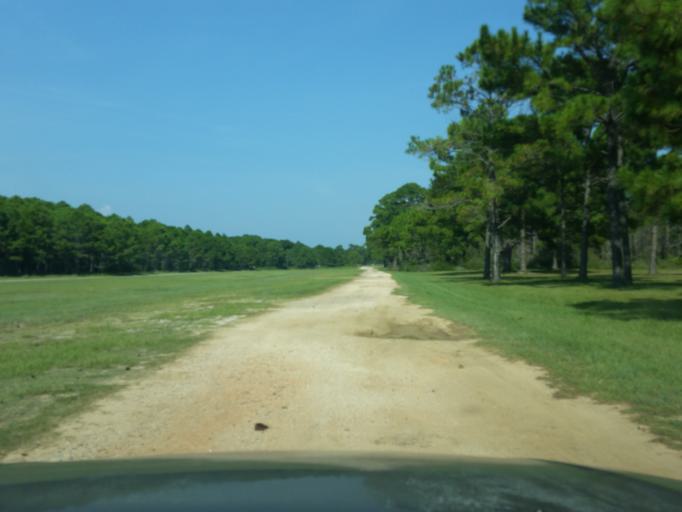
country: US
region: Alabama
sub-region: Mobile County
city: Dauphin Island
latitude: 30.2293
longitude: -88.0163
